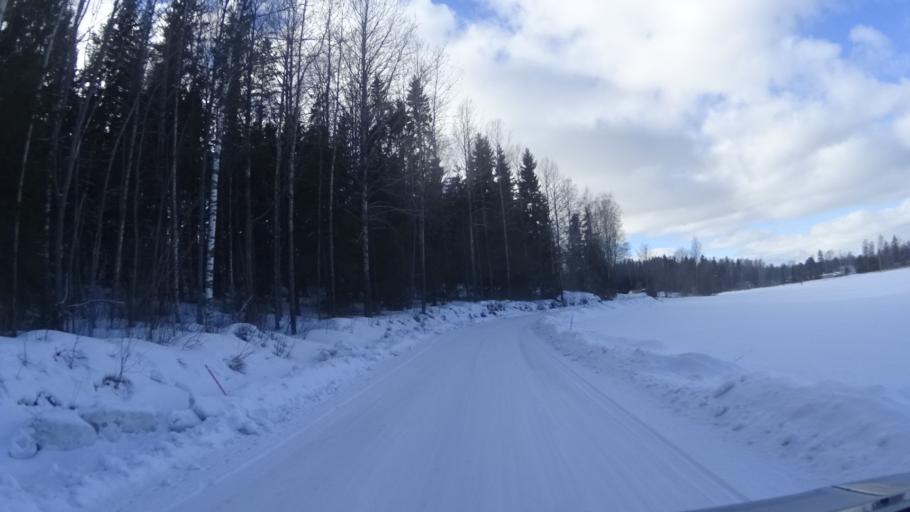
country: FI
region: Uusimaa
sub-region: Helsinki
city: Vantaa
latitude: 60.2481
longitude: 25.1684
